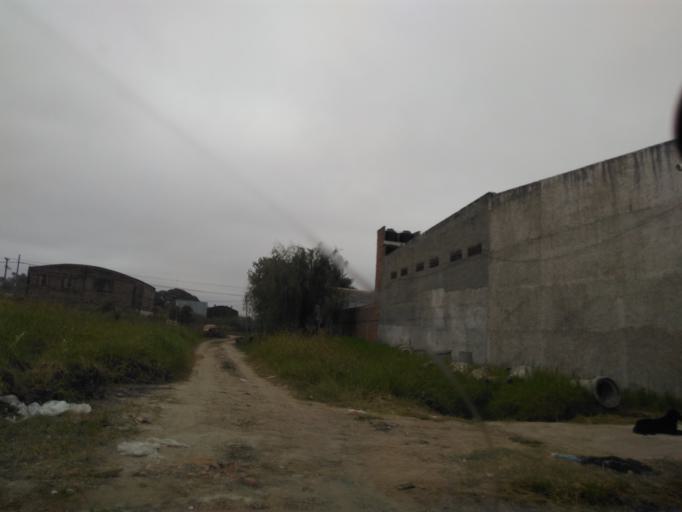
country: AR
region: Chaco
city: Fontana
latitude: -27.4510
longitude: -59.0311
